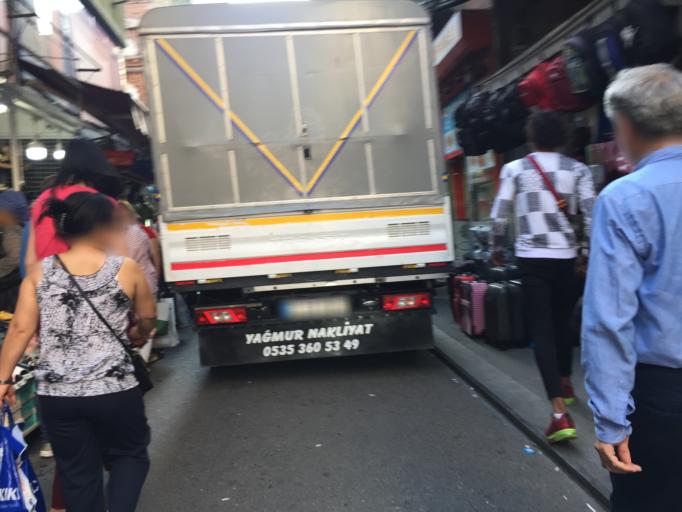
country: TR
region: Istanbul
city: Istanbul
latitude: 41.0062
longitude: 28.9561
